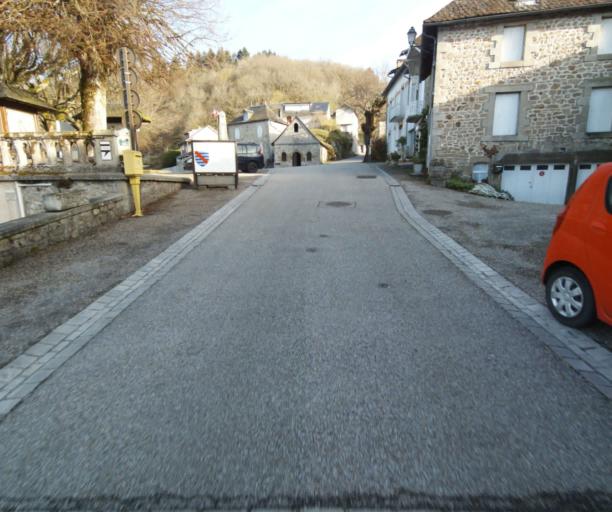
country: FR
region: Limousin
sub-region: Departement de la Correze
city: Correze
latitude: 45.2996
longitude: 1.8509
